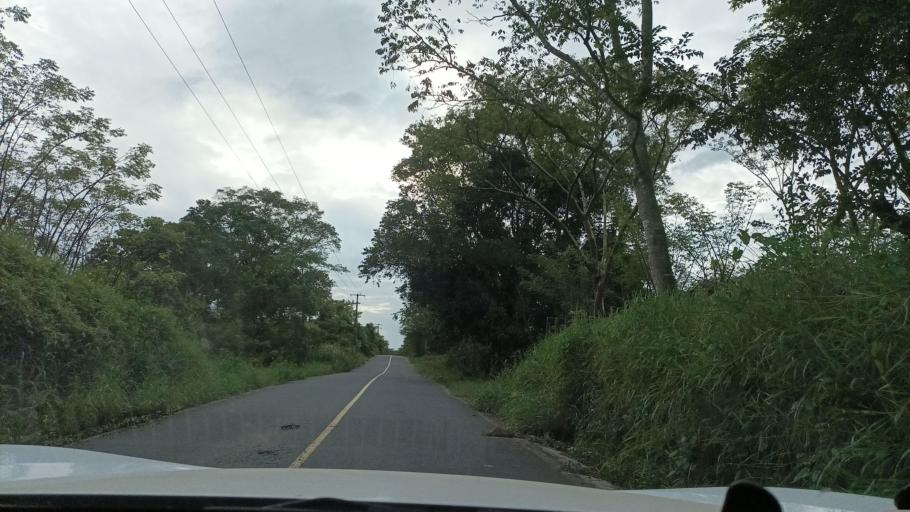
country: MX
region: Veracruz
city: Hidalgotitlan
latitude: 17.7171
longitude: -94.4764
